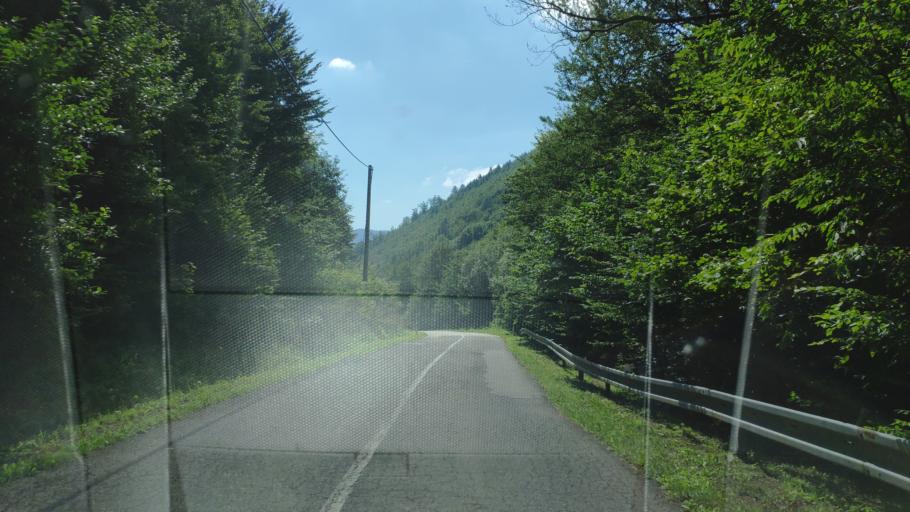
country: PL
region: Subcarpathian Voivodeship
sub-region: Powiat leski
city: Cisna
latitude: 49.0651
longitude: 22.3624
